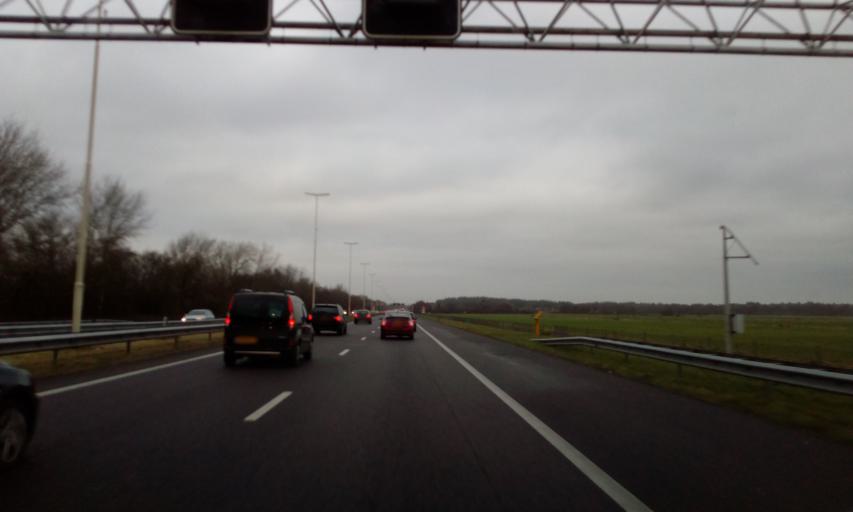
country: NL
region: North Holland
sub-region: Gemeente Wijdemeren
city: Nieuw-Loosdrecht
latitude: 52.1638
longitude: 5.1717
